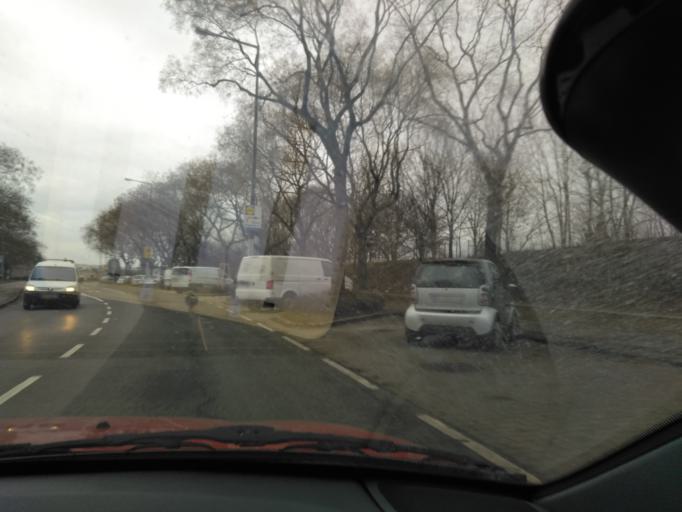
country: AT
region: Lower Austria
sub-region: Politischer Bezirk Modling
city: Vosendorf
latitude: 48.1647
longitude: 16.3357
